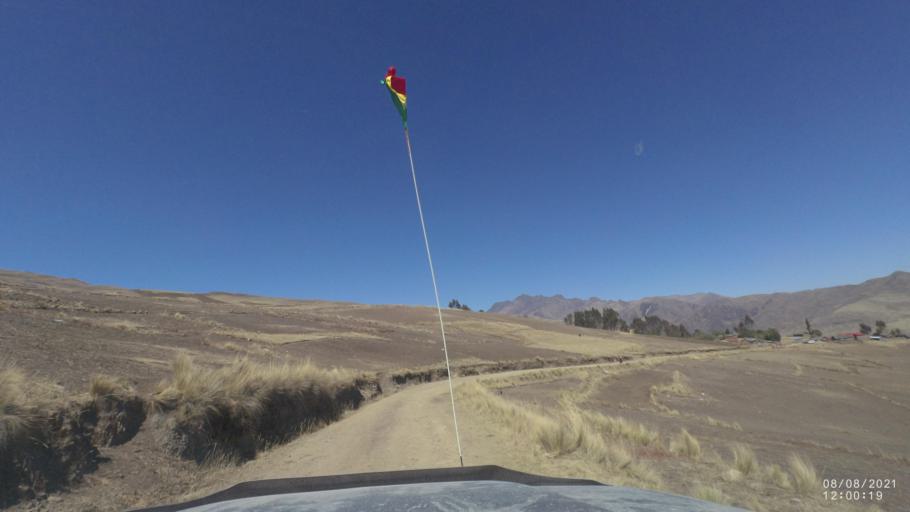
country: BO
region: Cochabamba
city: Colchani
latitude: -16.8364
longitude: -66.6265
